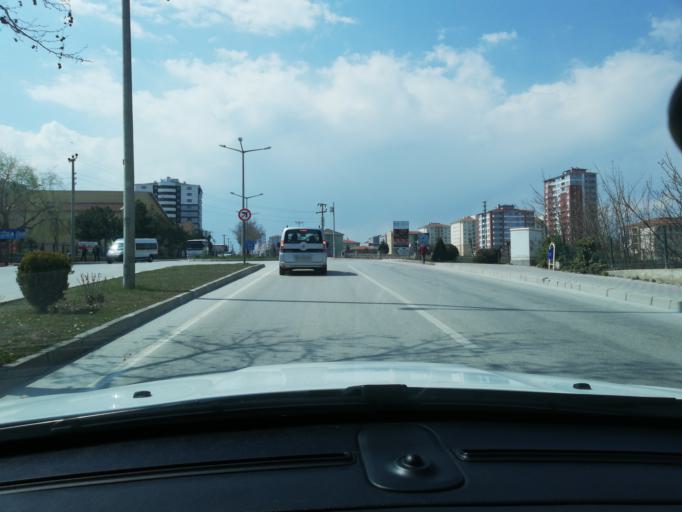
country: TR
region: Kastamonu
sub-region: Cide
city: Kastamonu
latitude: 41.4295
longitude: 33.7942
